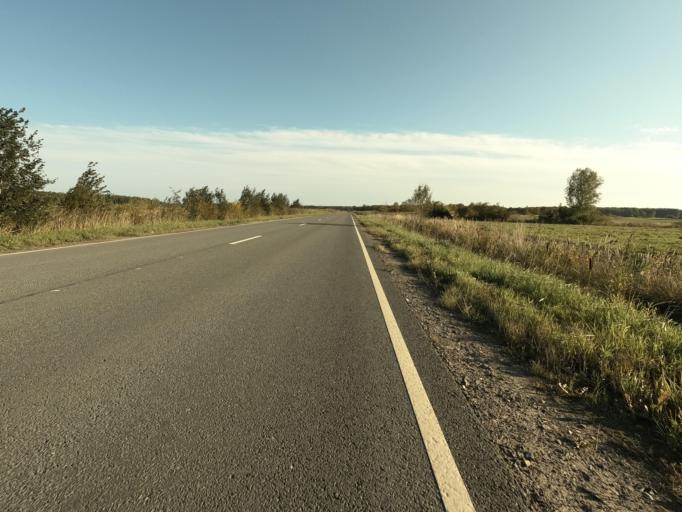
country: RU
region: St.-Petersburg
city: Sapernyy
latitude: 59.7359
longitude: 30.6552
